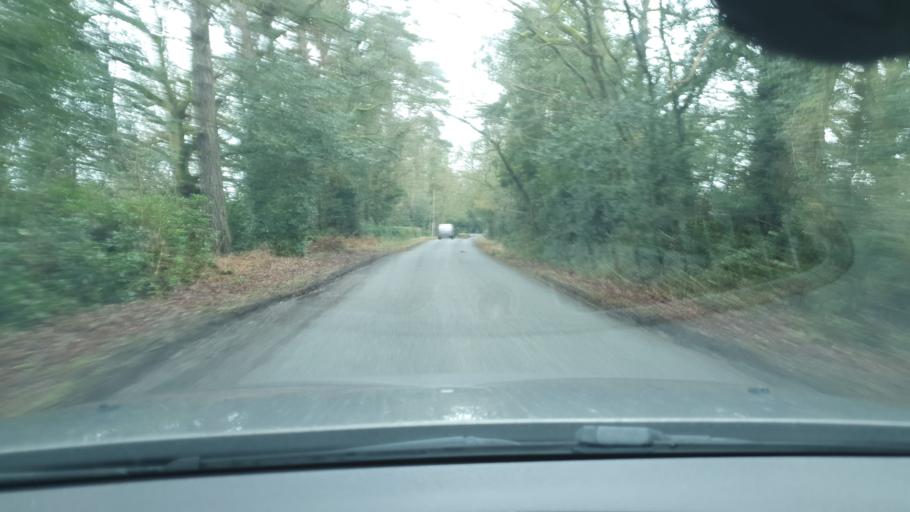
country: GB
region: England
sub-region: West Berkshire
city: Greenham
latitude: 51.3620
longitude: -1.3067
